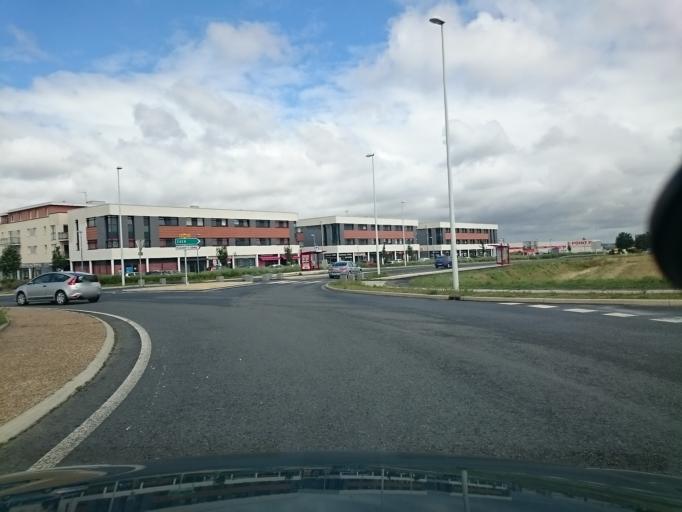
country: FR
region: Lower Normandy
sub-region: Departement du Calvados
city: Fleury-sur-Orne
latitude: 49.1394
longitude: -0.3757
